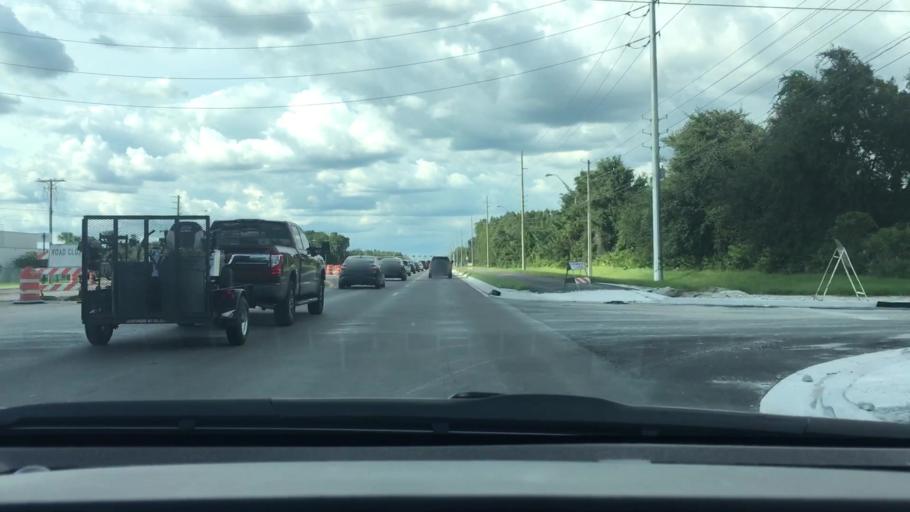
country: US
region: Florida
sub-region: Hillsborough County
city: Pebble Creek
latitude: 28.1565
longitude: -82.3533
